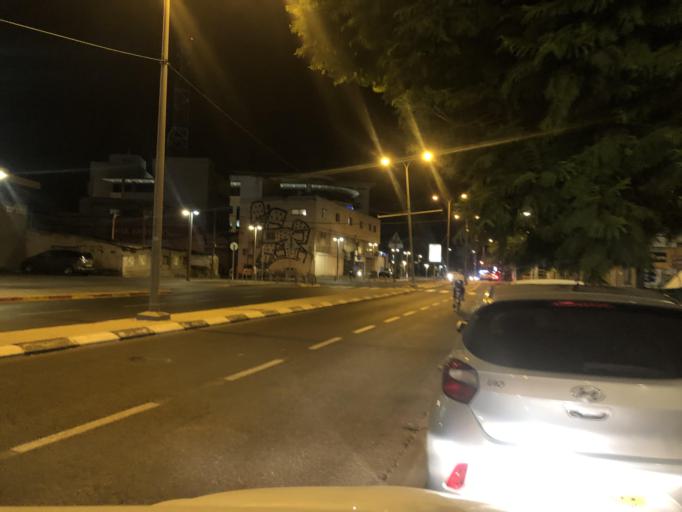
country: IL
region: Tel Aviv
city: Yafo
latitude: 32.0535
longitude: 34.7642
